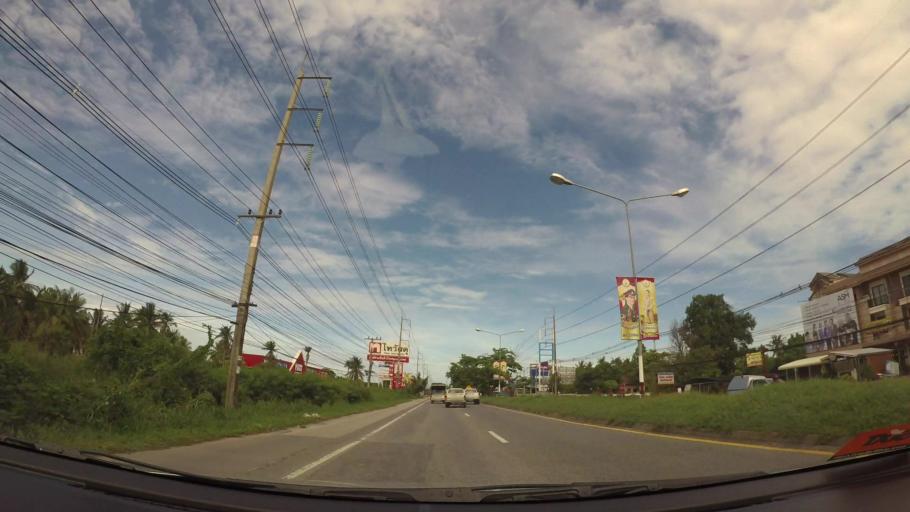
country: TH
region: Rayong
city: Ban Chang
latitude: 12.7359
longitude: 101.0778
